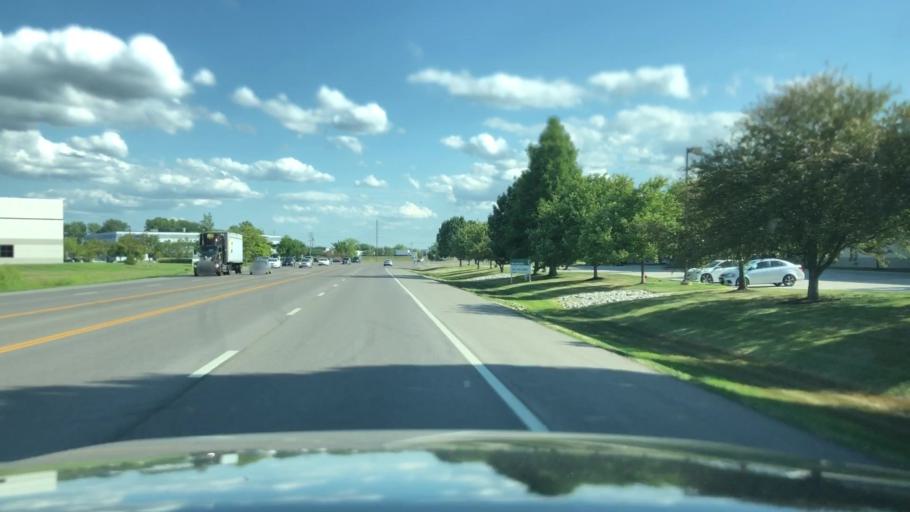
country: US
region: Missouri
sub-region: Saint Charles County
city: Saint Charles
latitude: 38.7835
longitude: -90.4592
